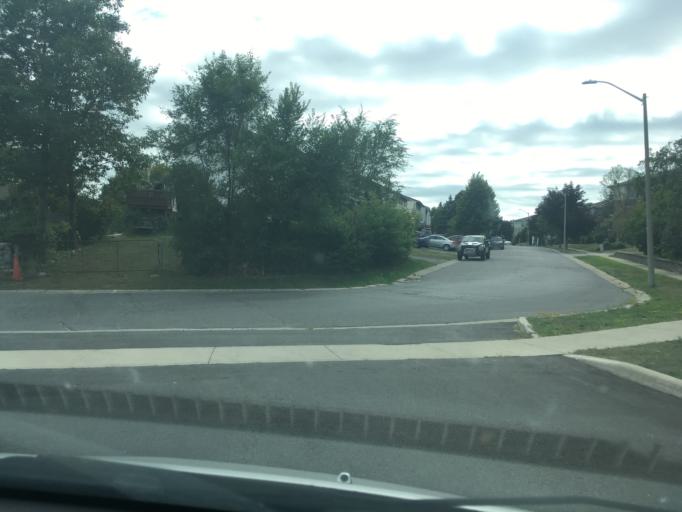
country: CA
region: Ontario
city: Kingston
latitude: 44.2749
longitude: -76.4781
